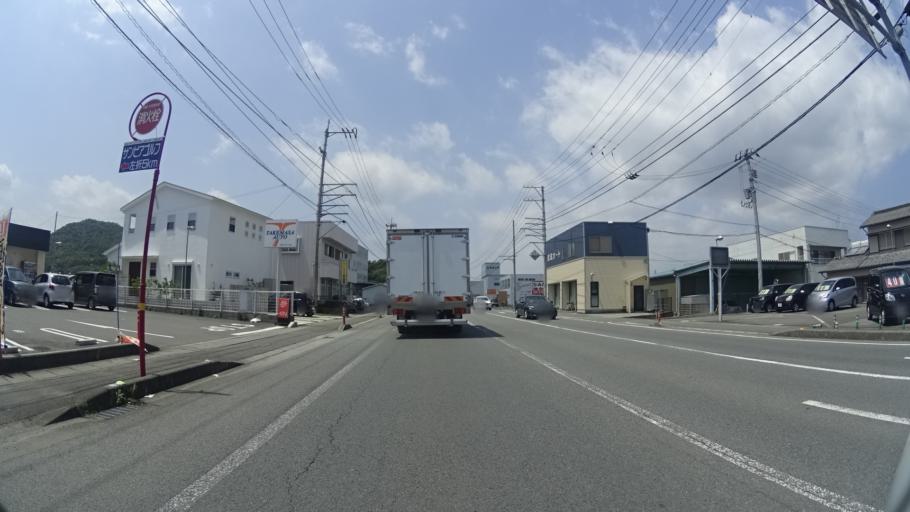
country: JP
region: Tokushima
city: Ishii
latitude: 34.0705
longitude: 134.4702
